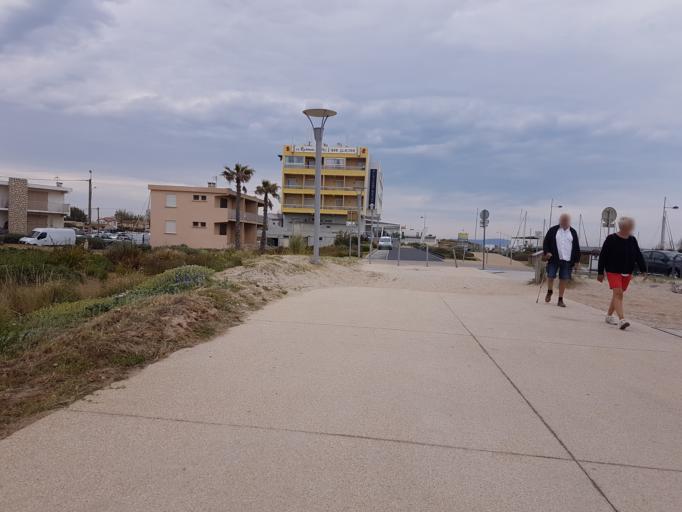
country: FR
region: Languedoc-Roussillon
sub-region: Departement de l'Herault
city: Marseillan
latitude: 43.3172
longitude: 3.5551
